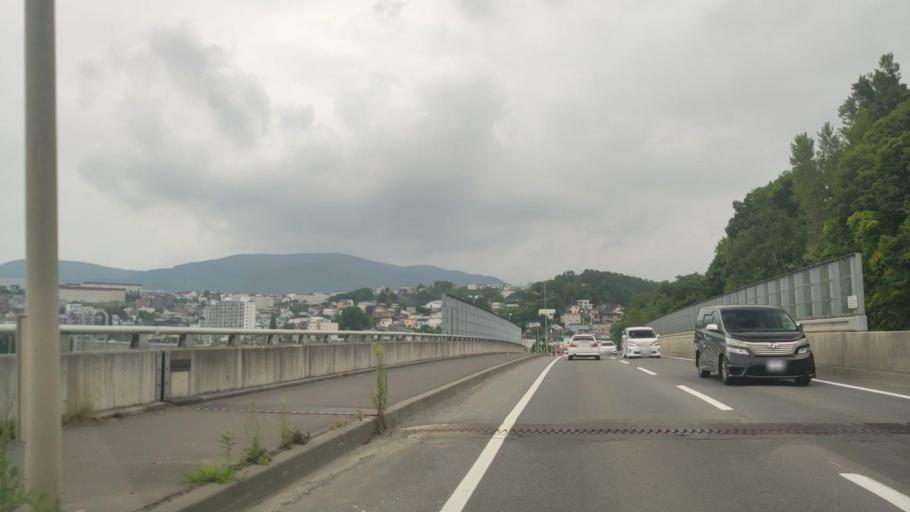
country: JP
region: Hokkaido
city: Otaru
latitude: 43.1807
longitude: 141.0371
